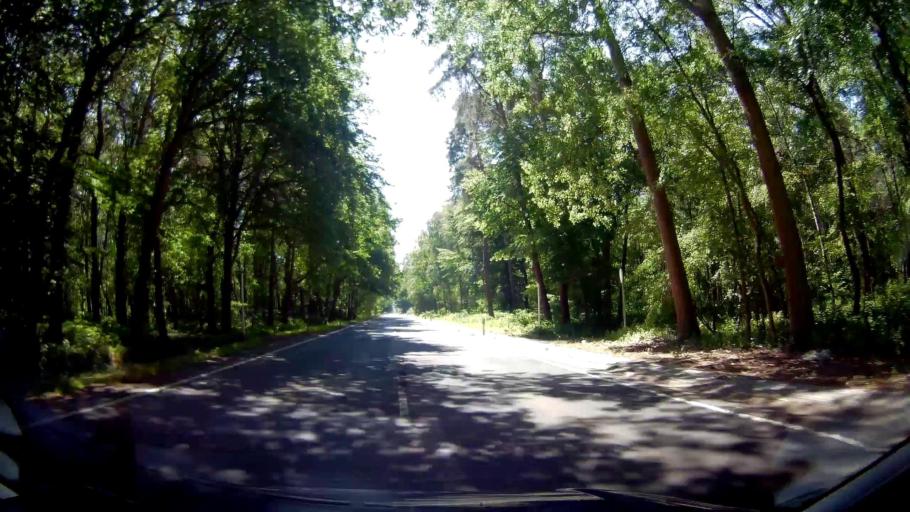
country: DE
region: North Rhine-Westphalia
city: Marl
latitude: 51.6412
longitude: 7.0455
